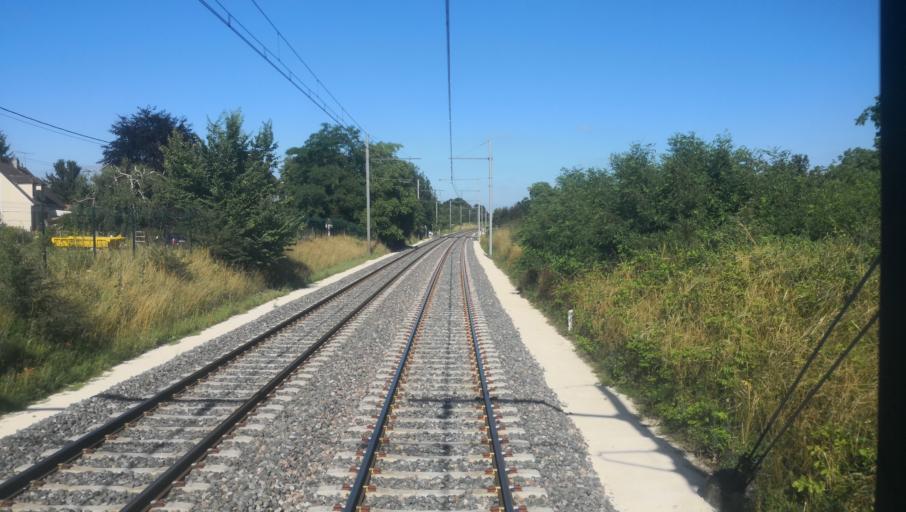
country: FR
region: Ile-de-France
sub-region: Departement de Seine-et-Marne
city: Bourron-Marlotte
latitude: 48.3368
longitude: 2.7125
